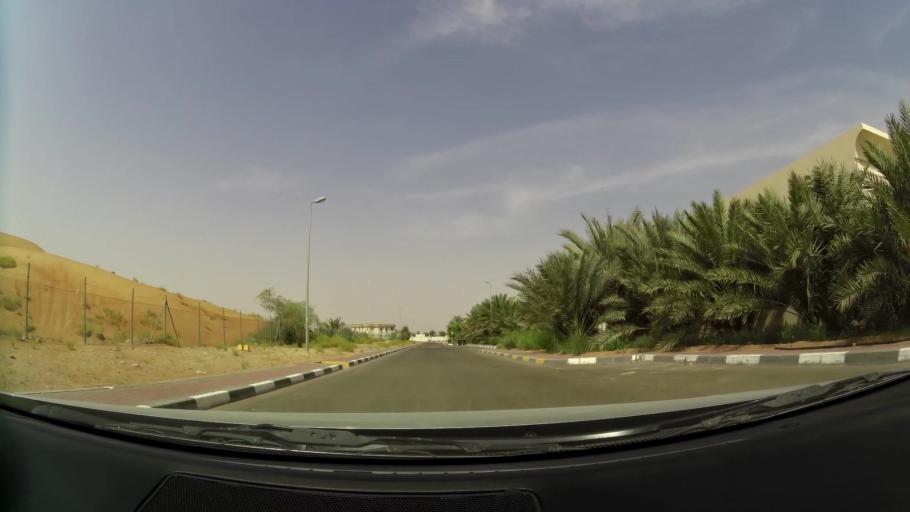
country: AE
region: Abu Dhabi
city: Al Ain
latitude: 24.1560
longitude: 55.6807
